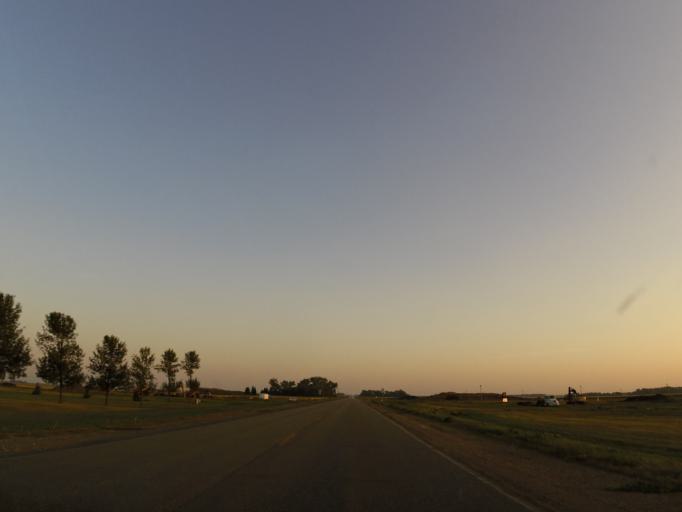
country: US
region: North Dakota
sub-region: Grand Forks County
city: Grand Forks
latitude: 47.8675
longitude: -97.0453
